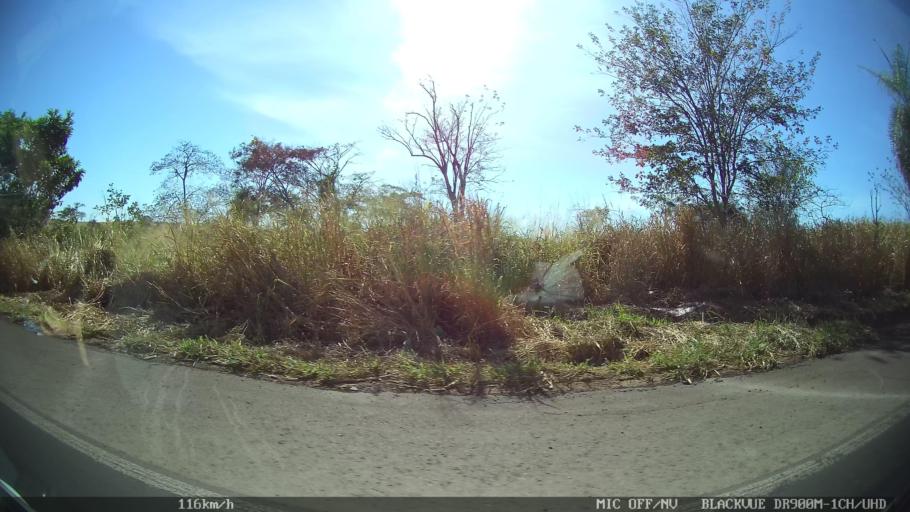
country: BR
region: Sao Paulo
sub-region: Barretos
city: Barretos
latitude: -20.6019
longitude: -48.7300
